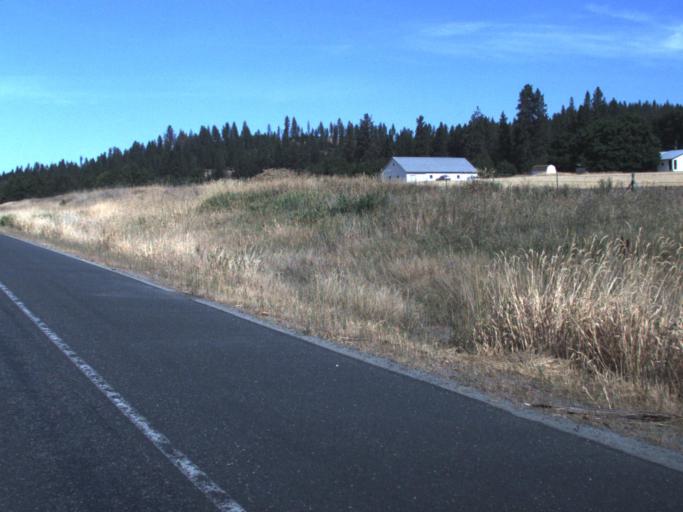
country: US
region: Washington
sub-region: Stevens County
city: Colville
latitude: 48.3882
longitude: -117.8443
